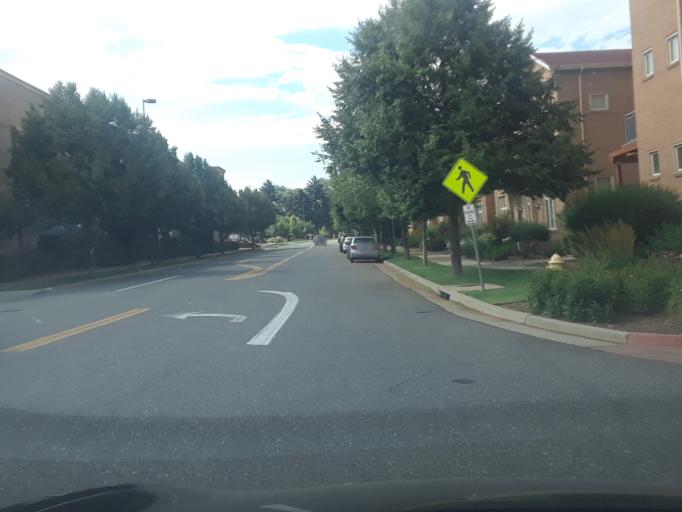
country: US
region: Colorado
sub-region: Arapahoe County
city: Glendale
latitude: 39.7201
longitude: -104.8999
